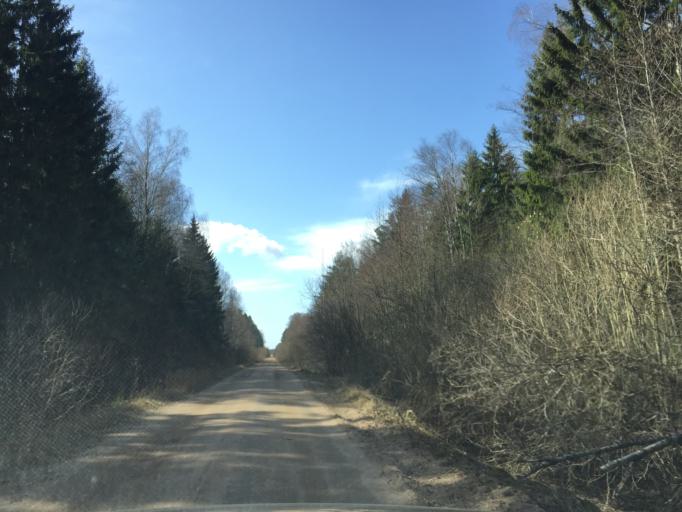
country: LV
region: Salaspils
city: Salaspils
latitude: 56.9231
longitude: 24.4375
